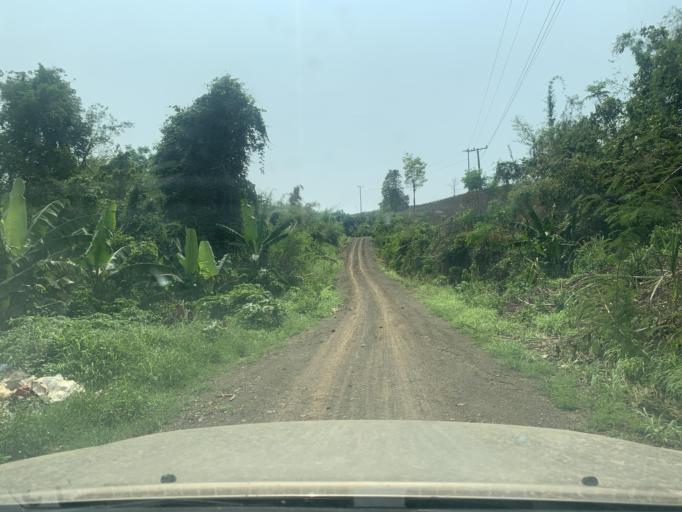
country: TH
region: Uttaradit
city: Ban Khok
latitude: 18.3710
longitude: 101.4019
